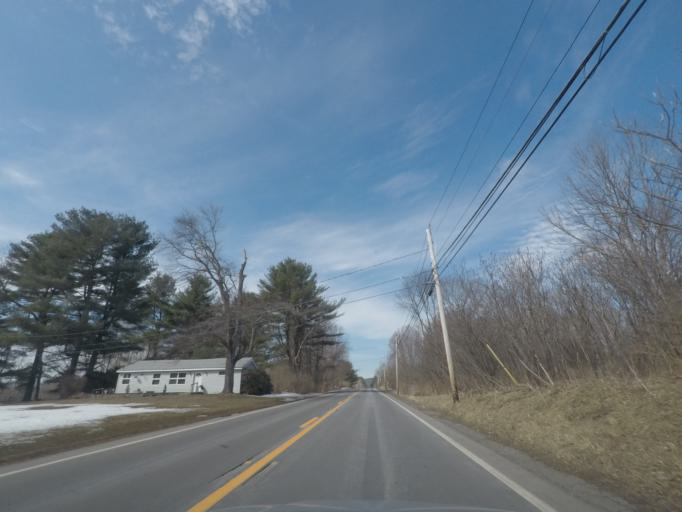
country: US
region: Massachusetts
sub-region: Berkshire County
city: West Stockbridge
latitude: 42.3427
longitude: -73.3762
